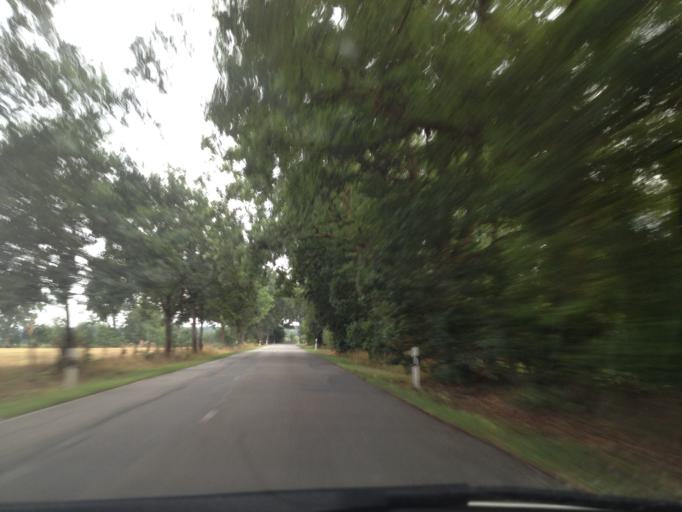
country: DE
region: Schleswig-Holstein
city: Daldorf
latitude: 54.0151
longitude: 10.2350
